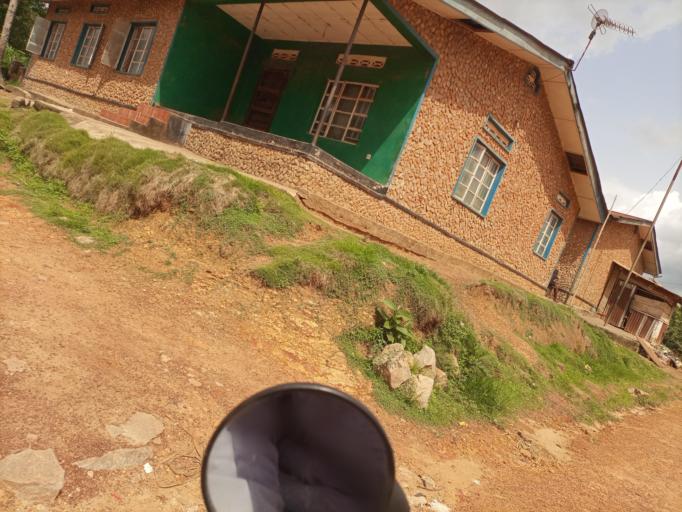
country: SL
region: Southern Province
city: Bo
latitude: 7.9476
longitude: -11.7362
